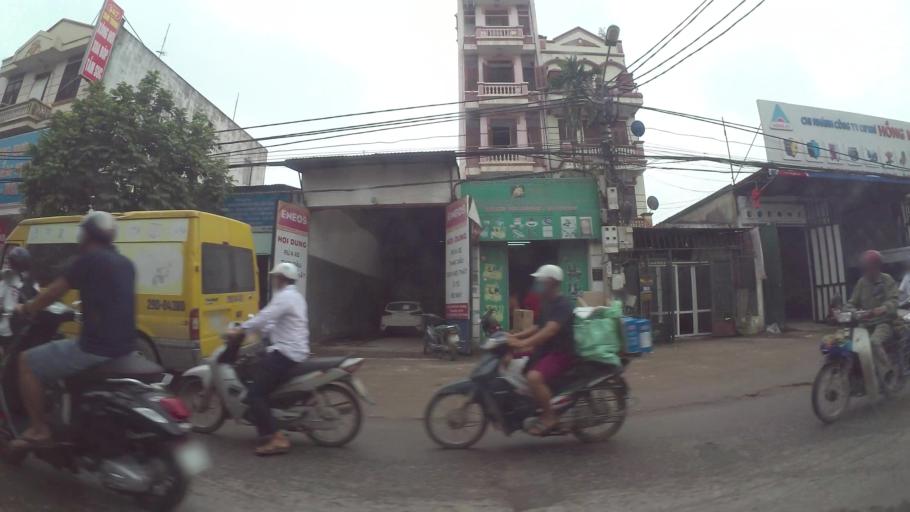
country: VN
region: Ha Noi
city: Hai BaTrung
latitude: 20.9799
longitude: 105.8647
